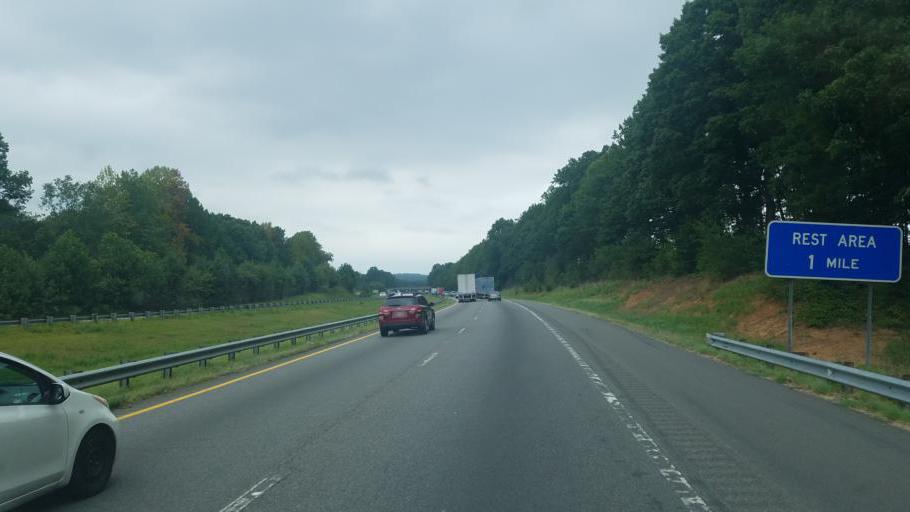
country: US
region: North Carolina
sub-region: Iredell County
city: Mooresville
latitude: 35.6151
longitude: -80.8574
